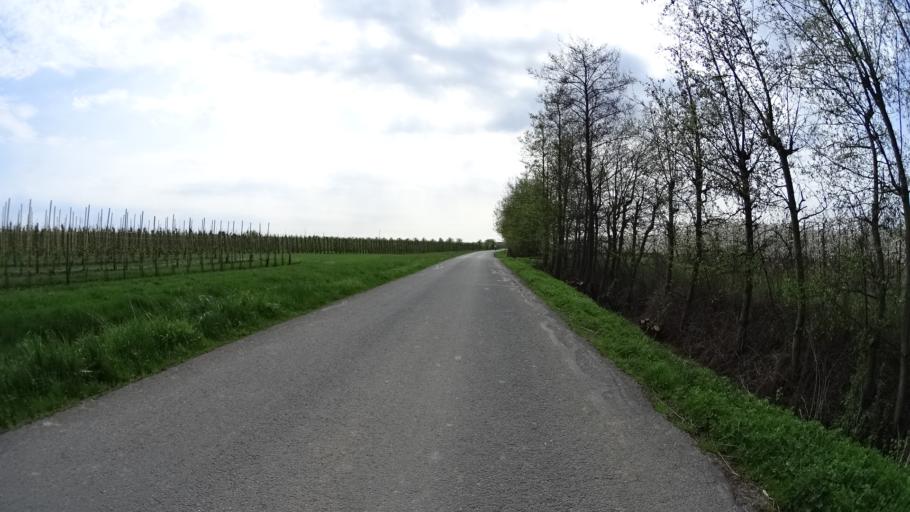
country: DE
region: Schleswig-Holstein
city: Wedel
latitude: 53.5439
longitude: 9.7421
